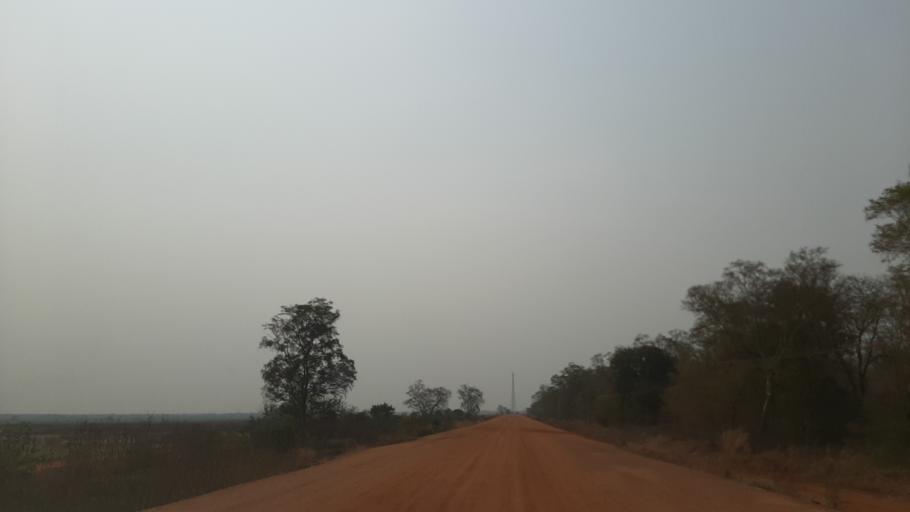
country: ET
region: Gambela
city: Gambela
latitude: 8.1534
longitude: 34.3486
